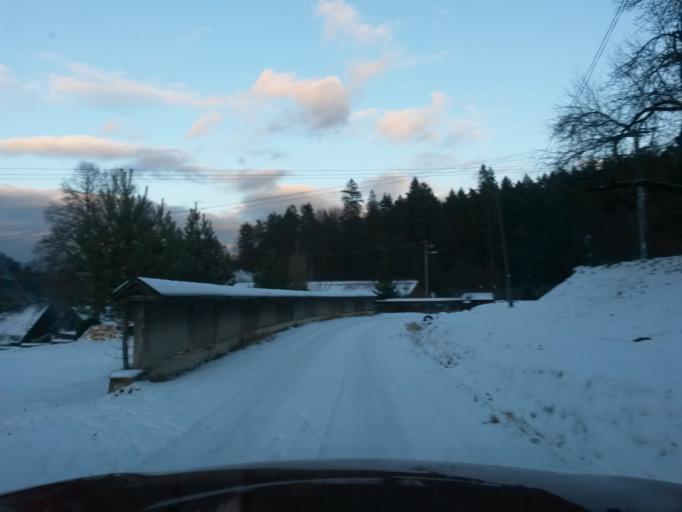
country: SK
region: Kosicky
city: Medzev
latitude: 48.7837
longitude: 20.7988
